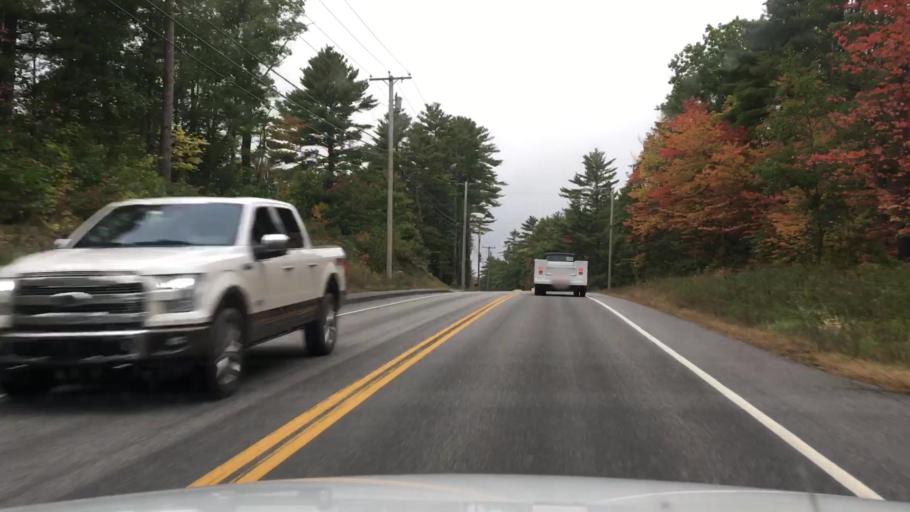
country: US
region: Maine
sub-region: Androscoggin County
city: Poland
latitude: 44.0660
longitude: -70.4002
